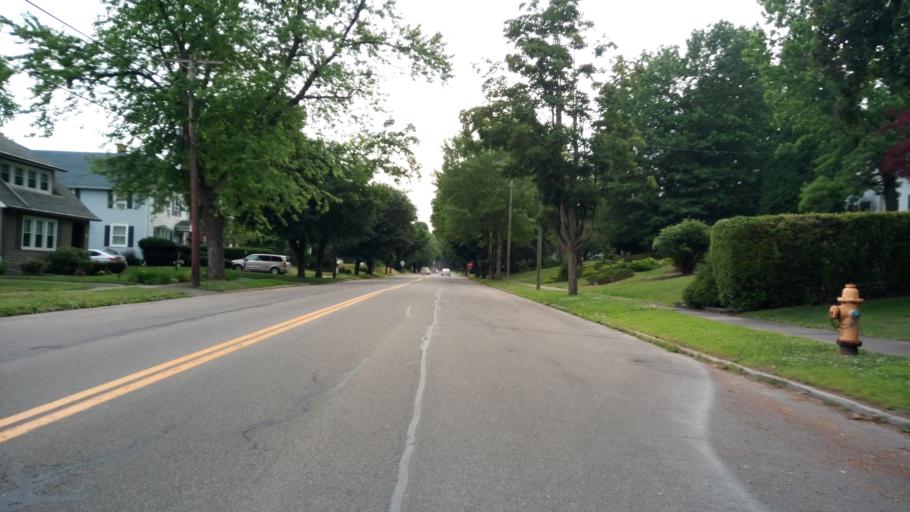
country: US
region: New York
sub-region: Chemung County
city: Elmira
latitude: 42.0894
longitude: -76.8264
